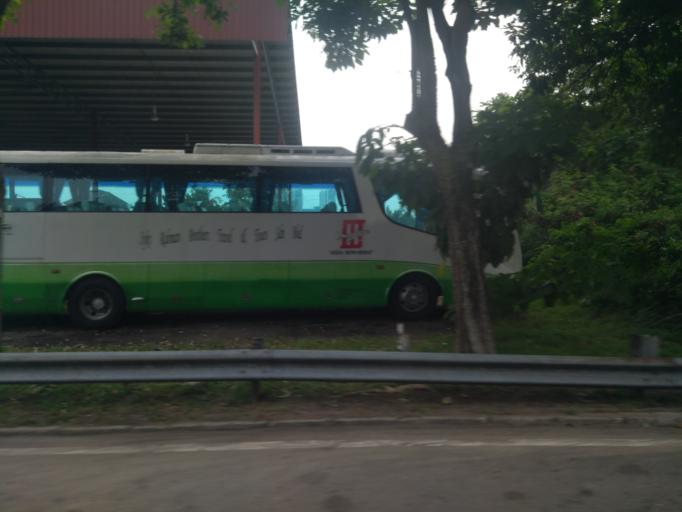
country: MY
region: Johor
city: Skudai
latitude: 1.4978
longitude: 103.6996
